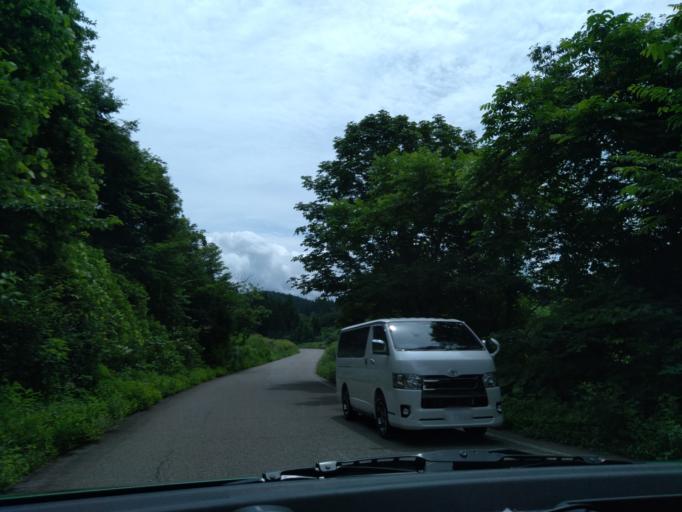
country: JP
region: Akita
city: Kakunodatemachi
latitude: 39.5724
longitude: 140.6328
